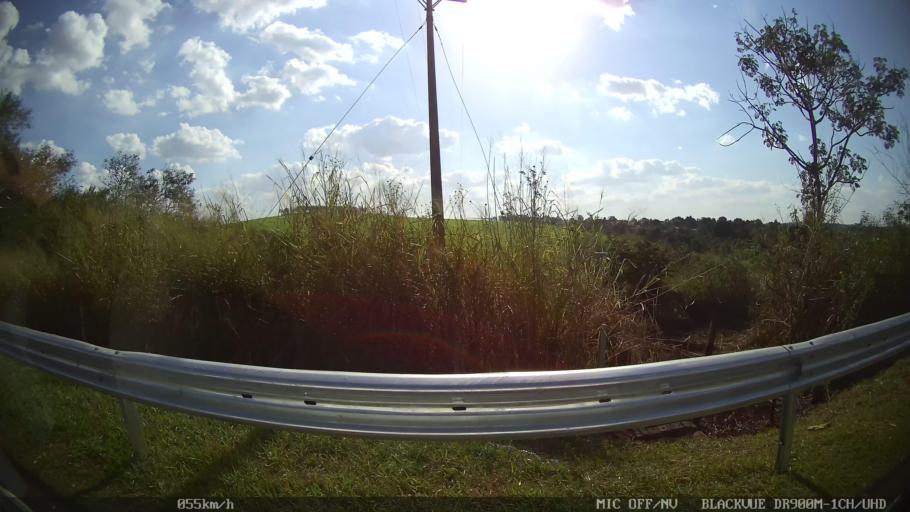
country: BR
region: Sao Paulo
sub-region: Ribeirao Preto
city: Ribeirao Preto
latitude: -21.1878
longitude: -47.8642
